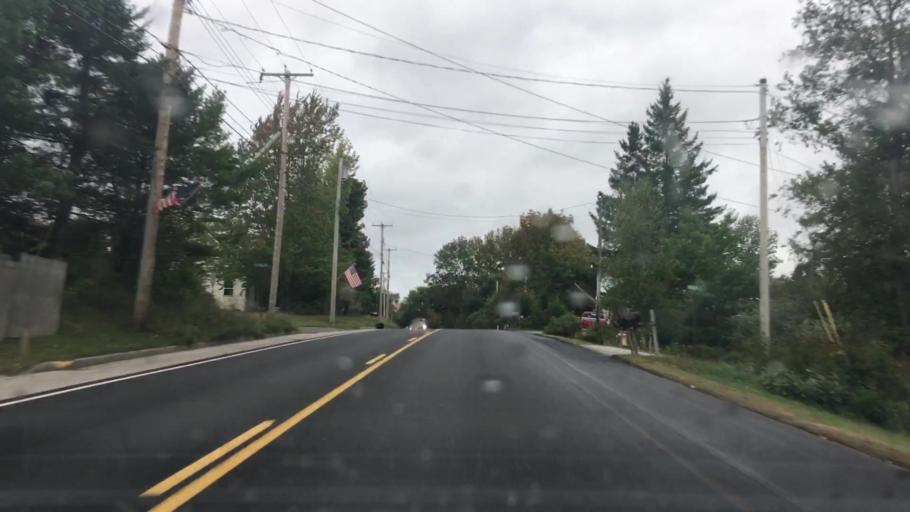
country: US
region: Maine
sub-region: Penobscot County
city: Orrington
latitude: 44.7521
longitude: -68.8018
